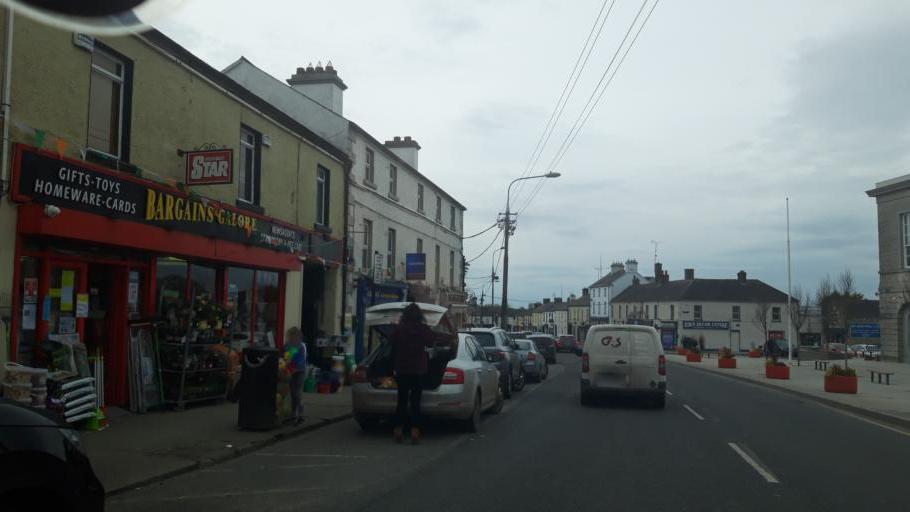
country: IE
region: Leinster
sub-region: Uibh Fhaili
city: Edenderry
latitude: 53.3430
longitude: -7.0485
